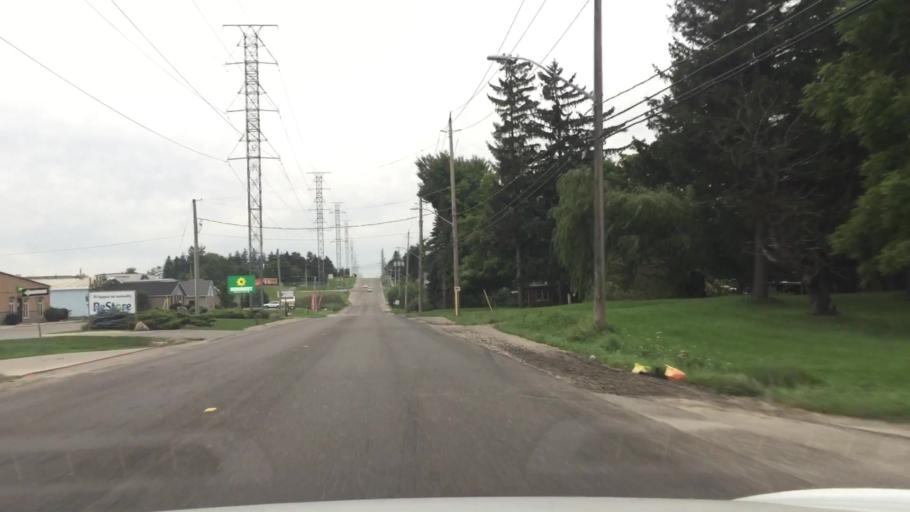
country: CA
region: Ontario
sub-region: Oxford County
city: Woodstock
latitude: 43.1231
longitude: -80.7198
